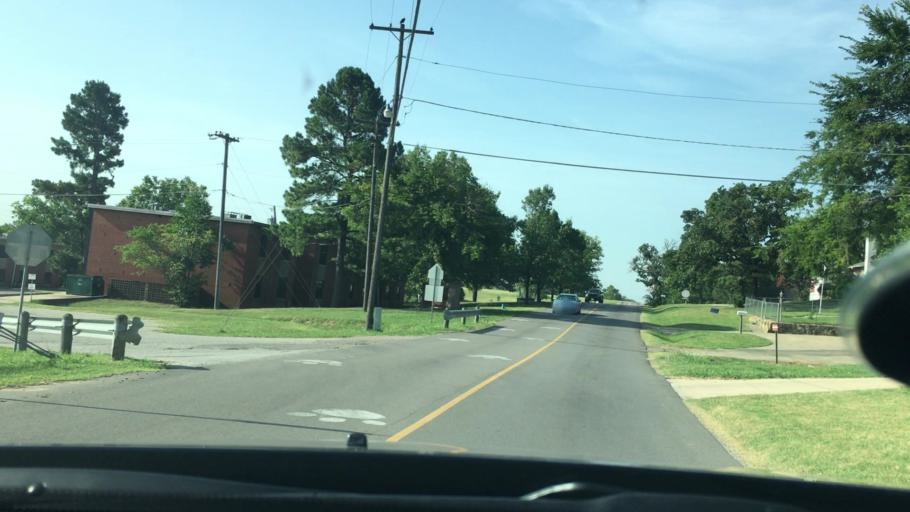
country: US
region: Oklahoma
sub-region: Pontotoc County
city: Ada
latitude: 34.7712
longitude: -96.6612
